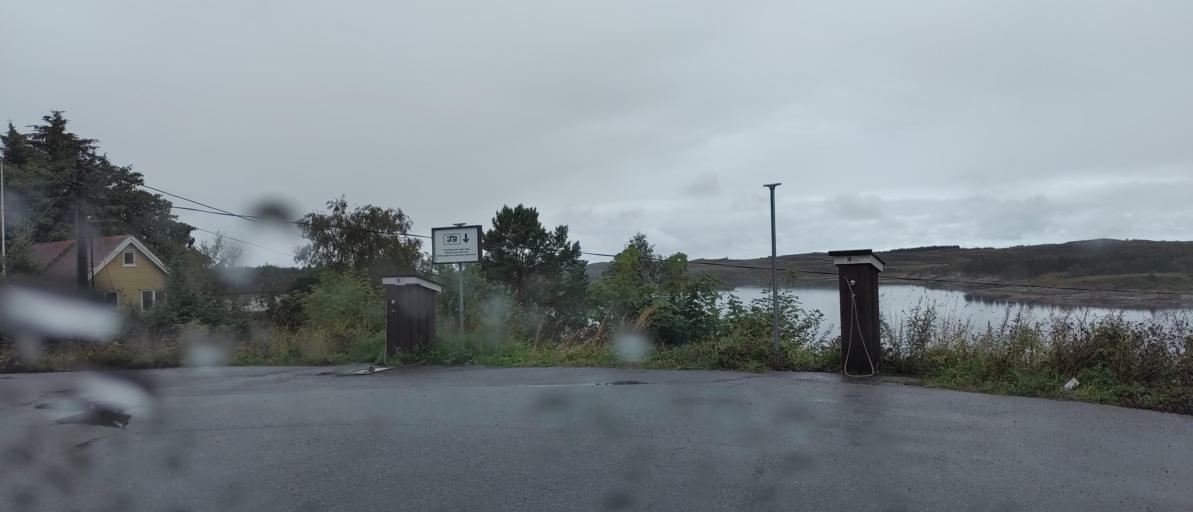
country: NO
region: More og Romsdal
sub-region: Eide
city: Eide
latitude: 63.0155
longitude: 7.4493
